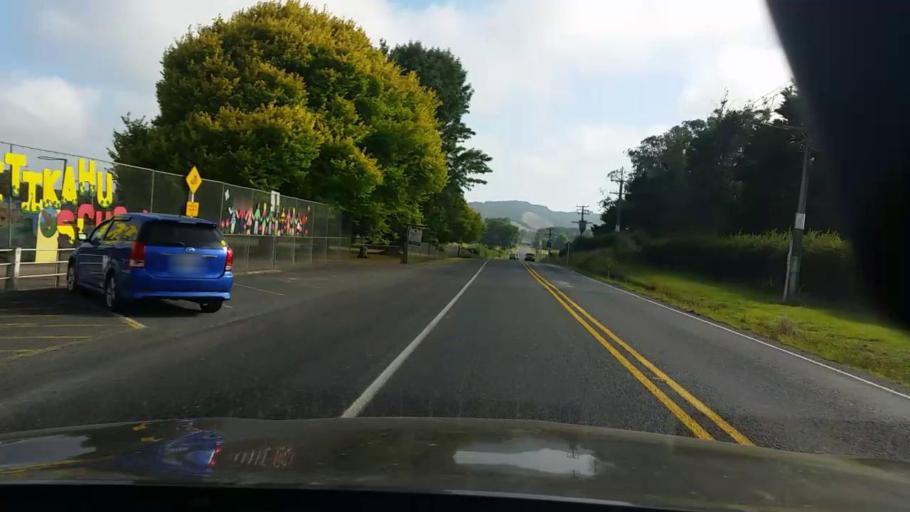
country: NZ
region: Waikato
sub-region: Hamilton City
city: Hamilton
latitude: -37.6115
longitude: 175.3460
